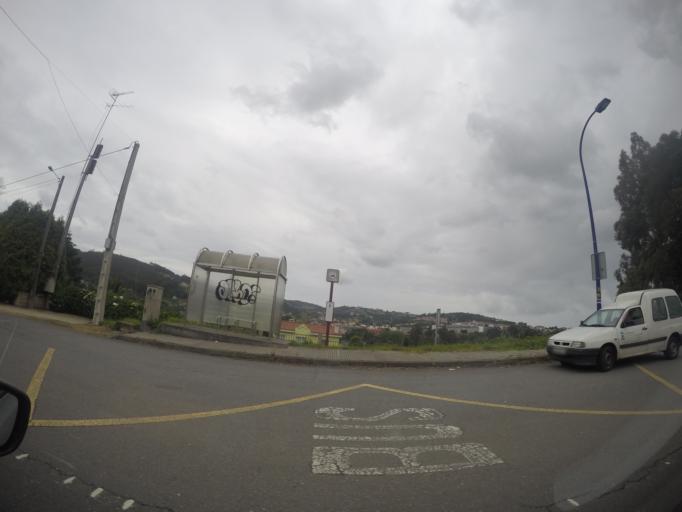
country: ES
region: Galicia
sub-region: Provincia da Coruna
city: Culleredo
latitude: 43.3079
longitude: -8.3765
